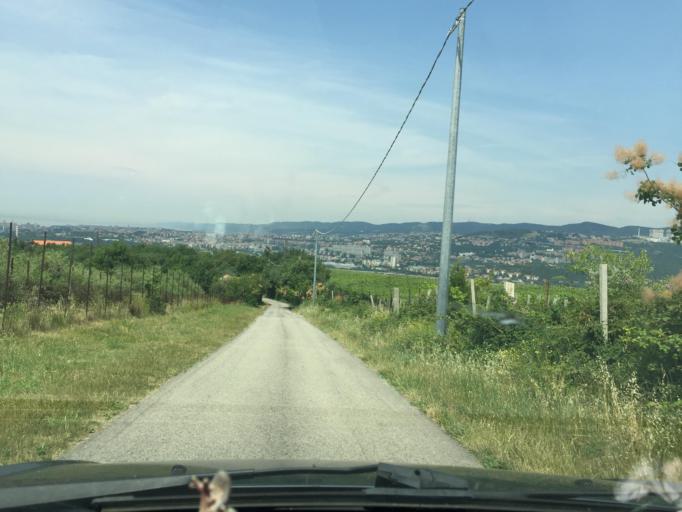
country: IT
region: Friuli Venezia Giulia
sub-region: Provincia di Trieste
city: Domio
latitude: 45.5987
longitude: 13.8208
